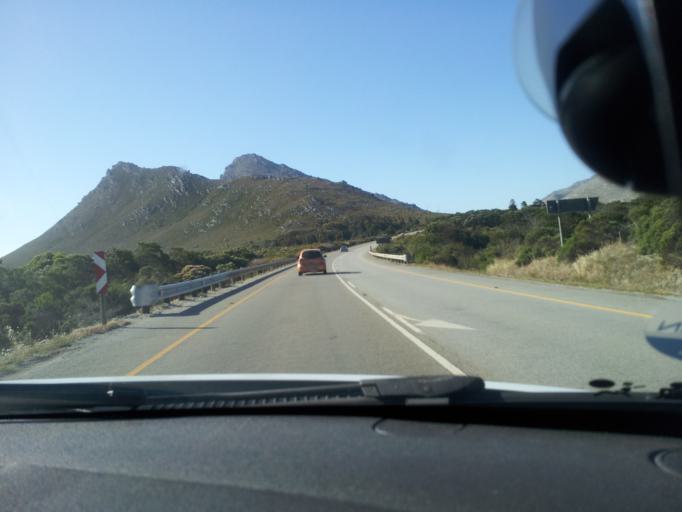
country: ZA
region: Western Cape
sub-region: Overberg District Municipality
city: Grabouw
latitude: -34.3391
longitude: 18.8426
